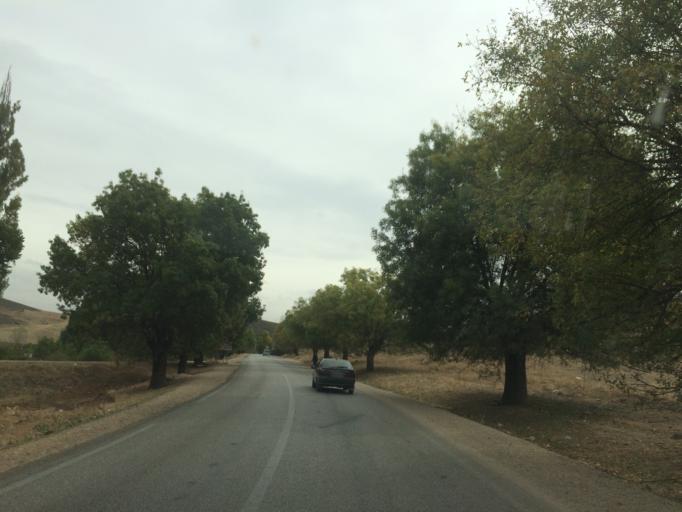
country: MA
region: Meknes-Tafilalet
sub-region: Ifrane
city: Azrou
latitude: 33.4743
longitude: -5.2476
